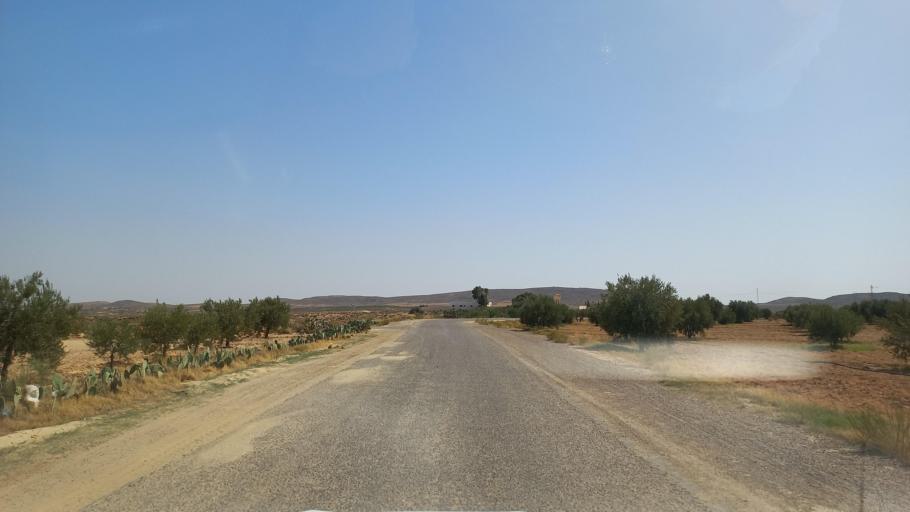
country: TN
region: Al Qasrayn
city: Kasserine
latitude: 35.2125
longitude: 9.0418
